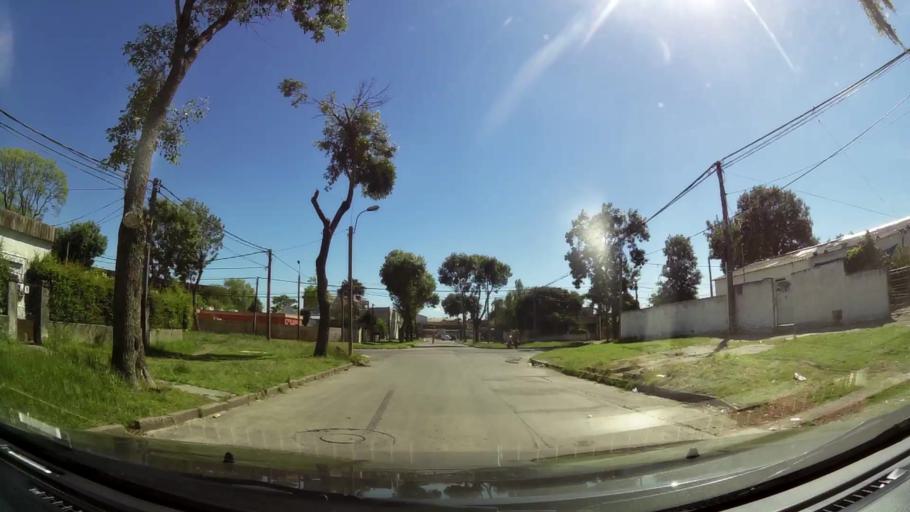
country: UY
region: Canelones
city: Paso de Carrasco
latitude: -34.8623
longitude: -56.1248
